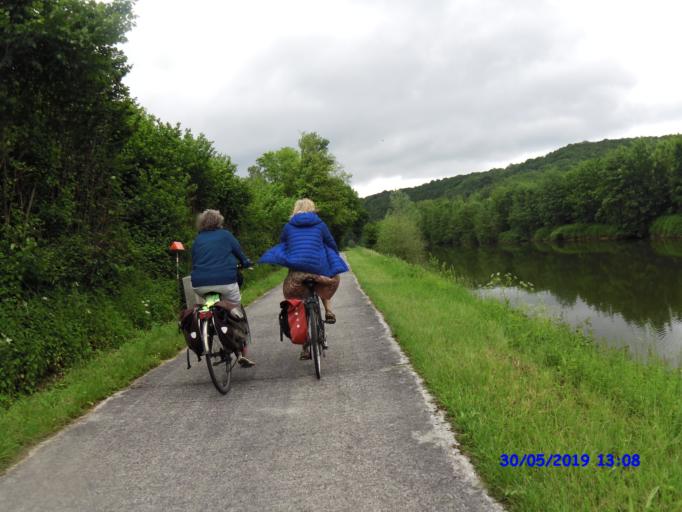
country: BE
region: Wallonia
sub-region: Province du Hainaut
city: Thuin
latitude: 50.3561
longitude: 4.3102
